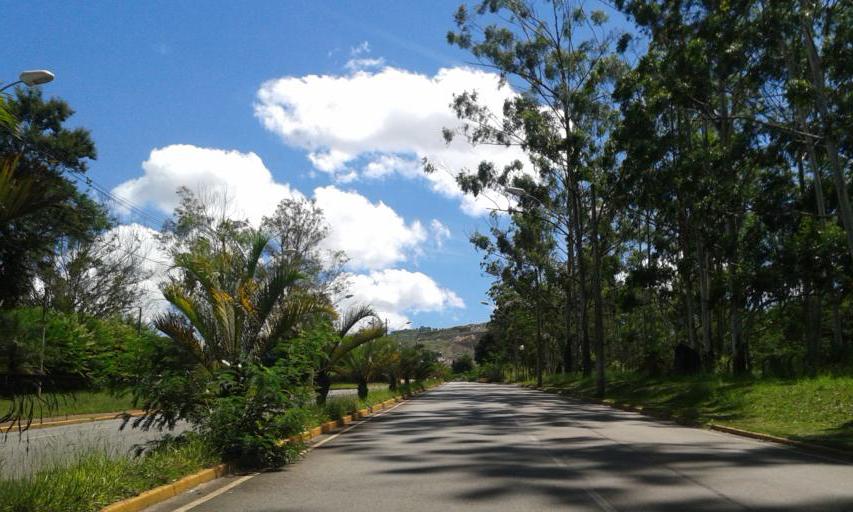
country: BR
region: Minas Gerais
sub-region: Itabira
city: Itabira
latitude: -19.6353
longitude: -43.2397
